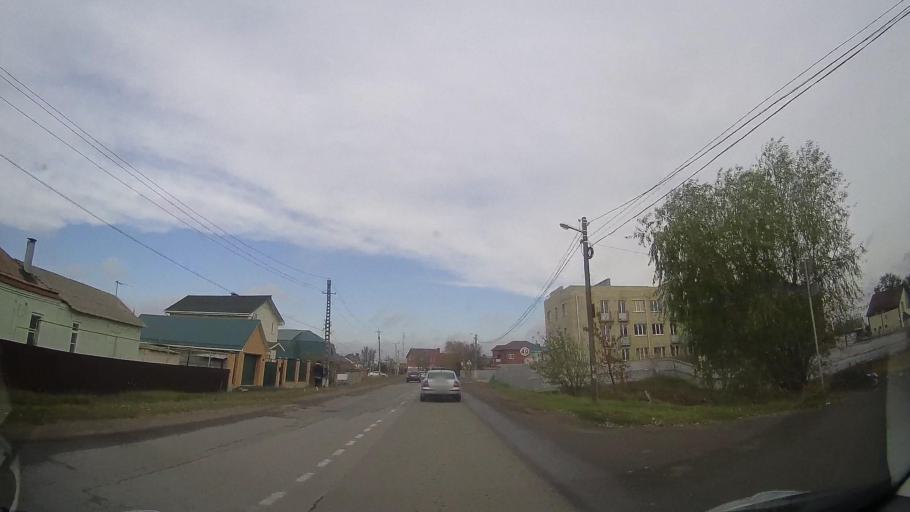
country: RU
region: Rostov
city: Bataysk
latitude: 47.1498
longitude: 39.7668
